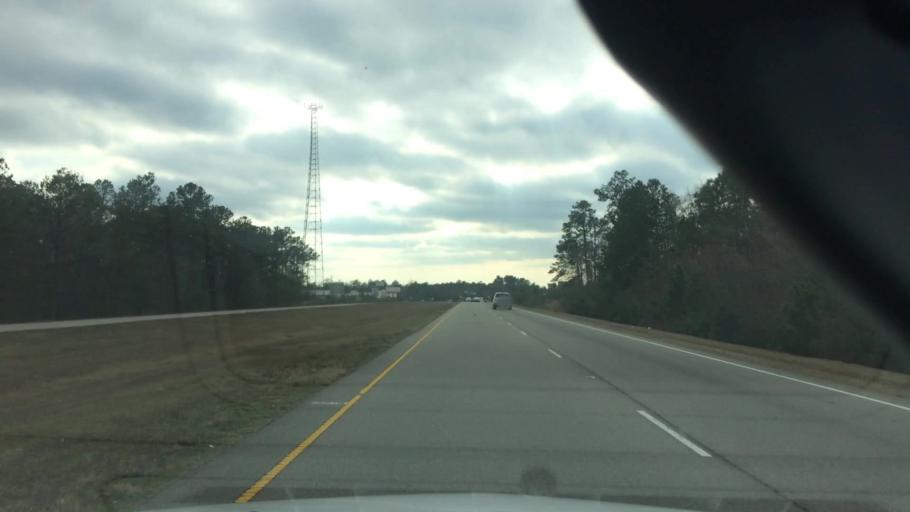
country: US
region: North Carolina
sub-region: Brunswick County
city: Shallotte
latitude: 33.9666
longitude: -78.4140
